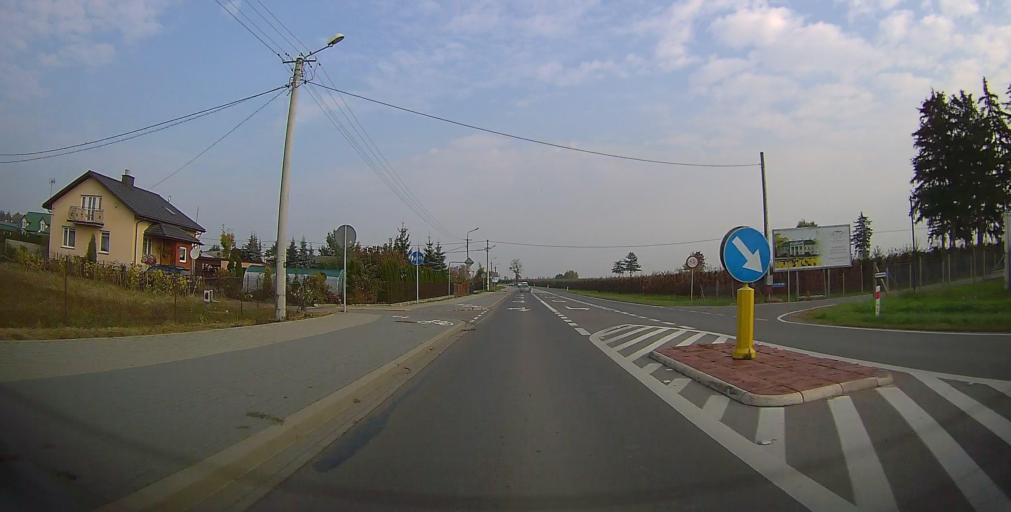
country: PL
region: Masovian Voivodeship
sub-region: Powiat grojecki
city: Mogielnica
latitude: 51.7105
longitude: 20.7419
